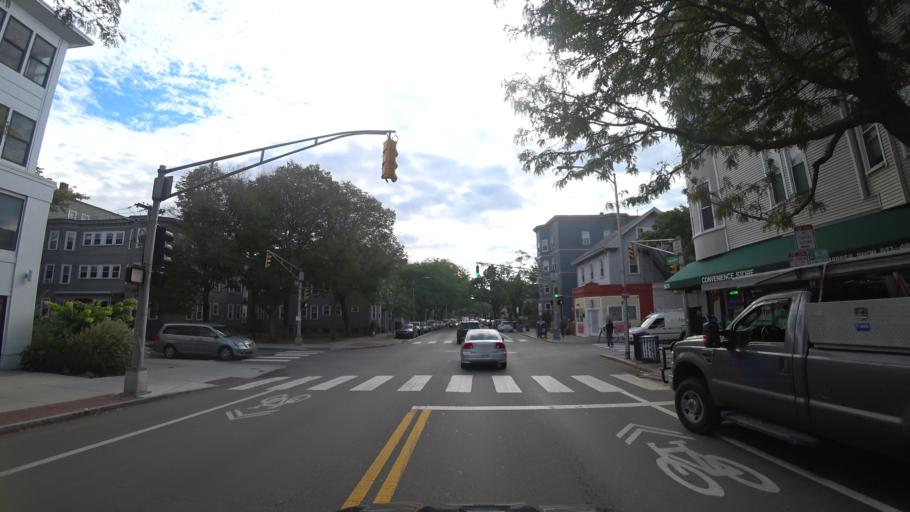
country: US
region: Massachusetts
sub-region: Middlesex County
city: Cambridge
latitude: 42.3680
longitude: -71.0977
